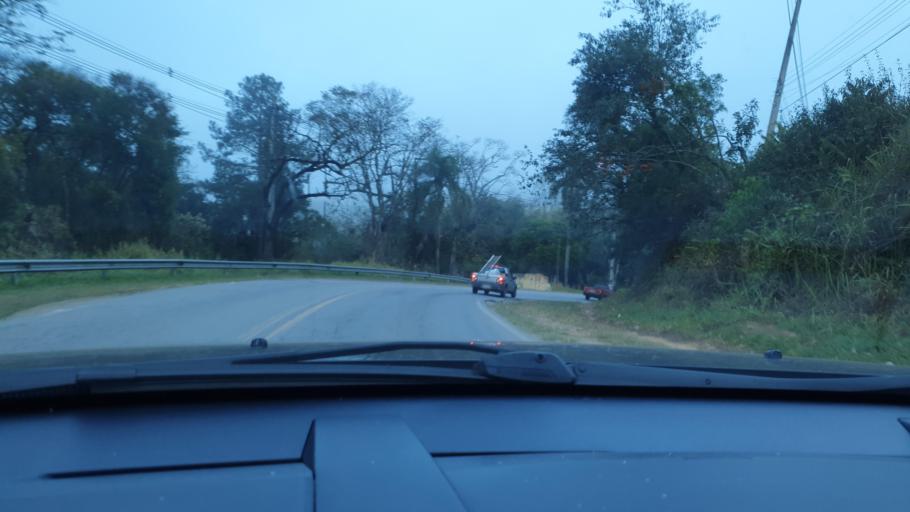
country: BR
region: Sao Paulo
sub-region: Ibiuna
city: Ibiuna
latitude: -23.6769
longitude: -47.2397
